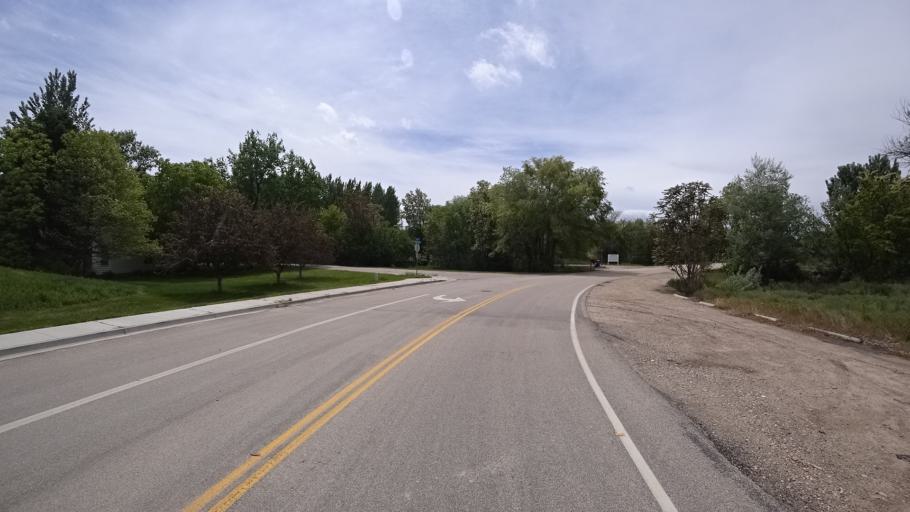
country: US
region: Idaho
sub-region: Ada County
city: Eagle
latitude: 43.6949
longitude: -116.4038
